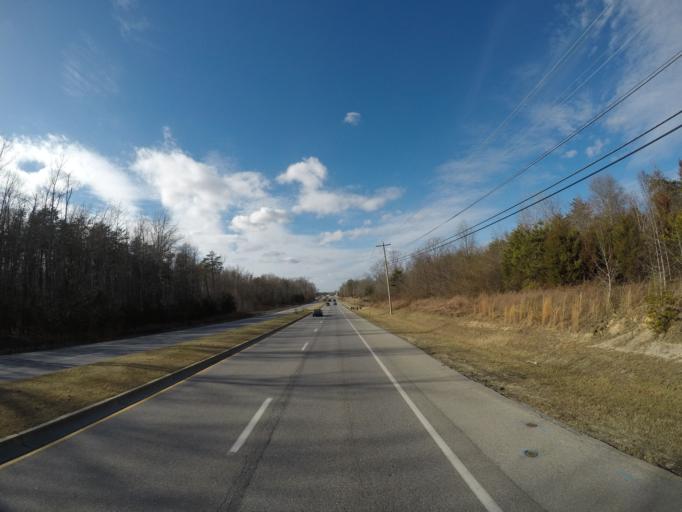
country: US
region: Maryland
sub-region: Charles County
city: Saint Charles
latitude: 38.6060
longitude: -76.9527
